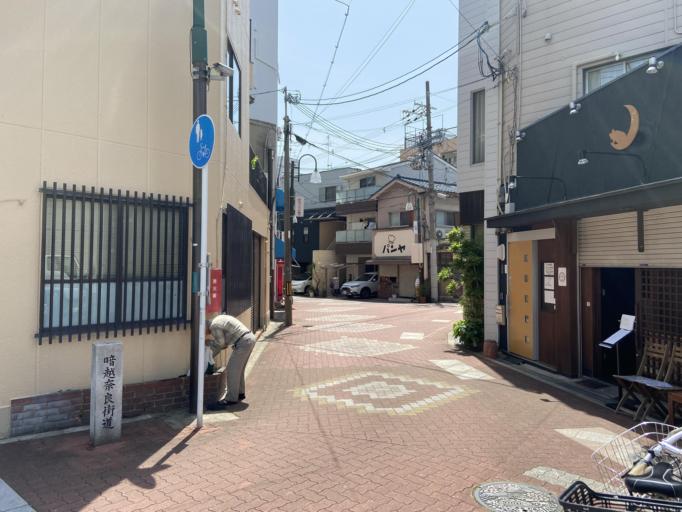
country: JP
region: Osaka
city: Osaka-shi
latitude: 34.6744
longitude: 135.5341
